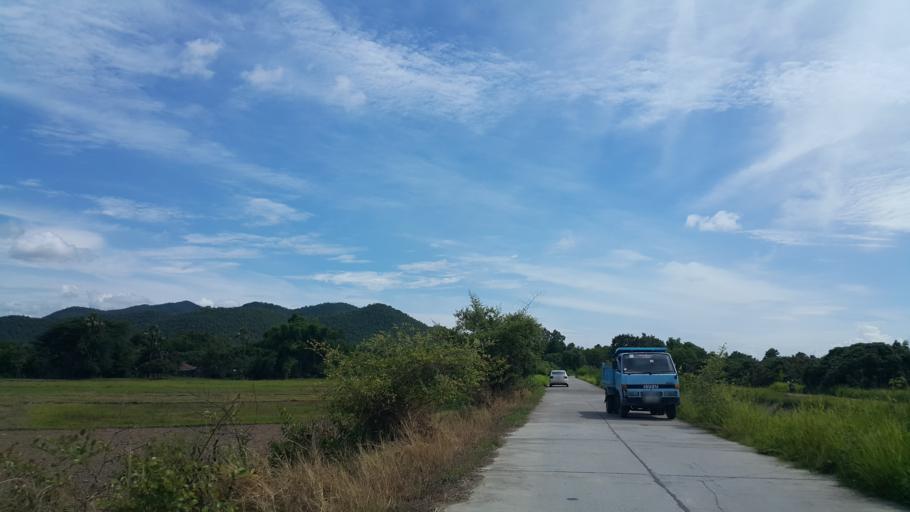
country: TH
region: Chiang Mai
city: Mae On
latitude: 18.7310
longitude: 99.1982
